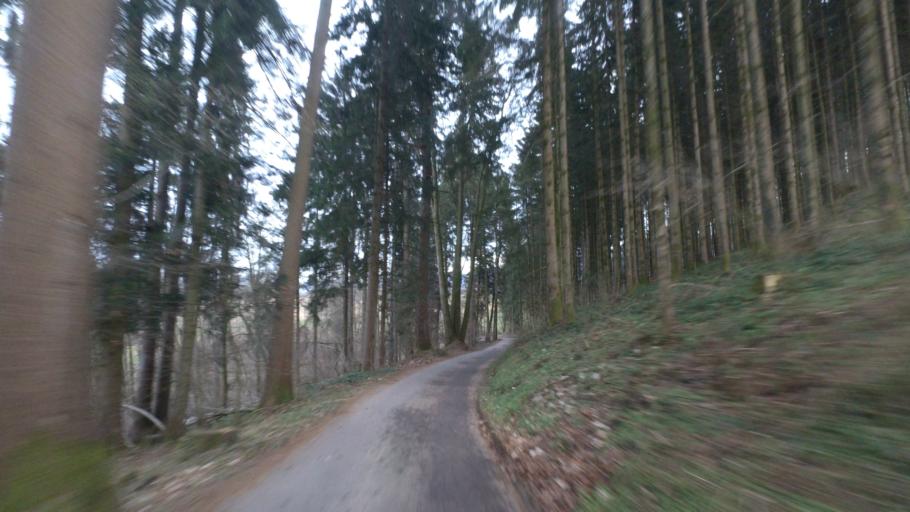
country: DE
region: Bavaria
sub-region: Upper Bavaria
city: Ubersee
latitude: 47.8077
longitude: 12.5213
